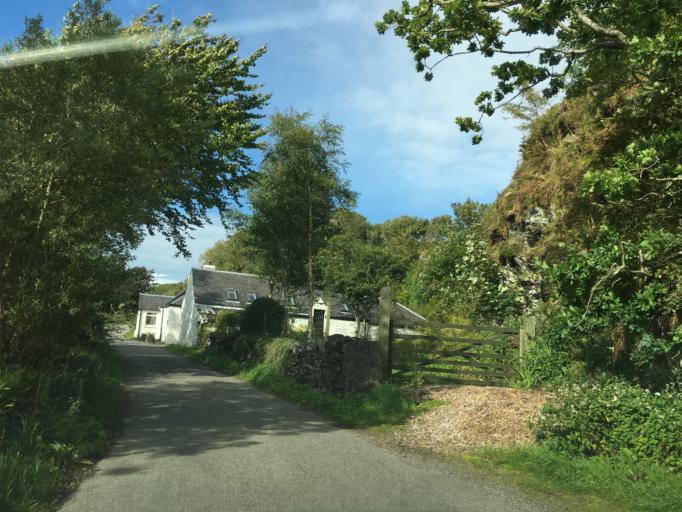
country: GB
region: Scotland
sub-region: Argyll and Bute
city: Oban
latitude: 56.2690
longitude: -5.6281
